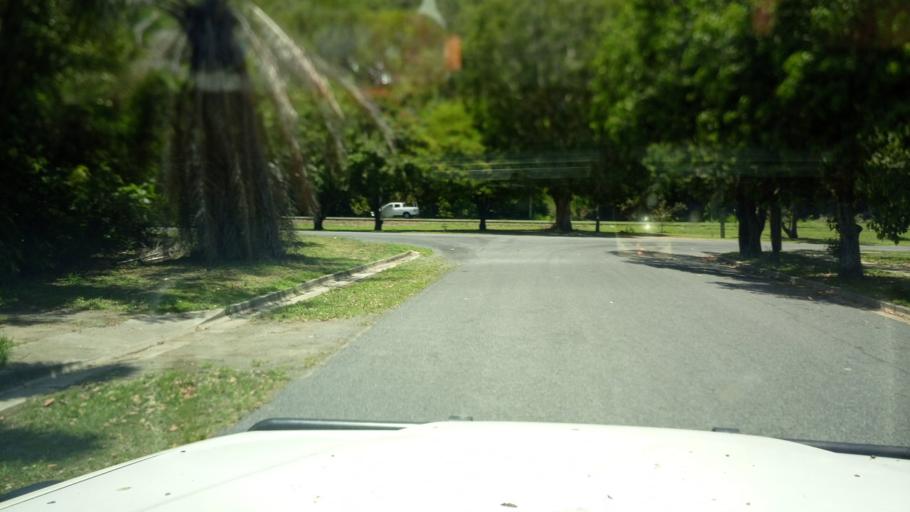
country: AU
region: Queensland
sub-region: Cairns
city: Redlynch
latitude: -16.8752
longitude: 145.7414
